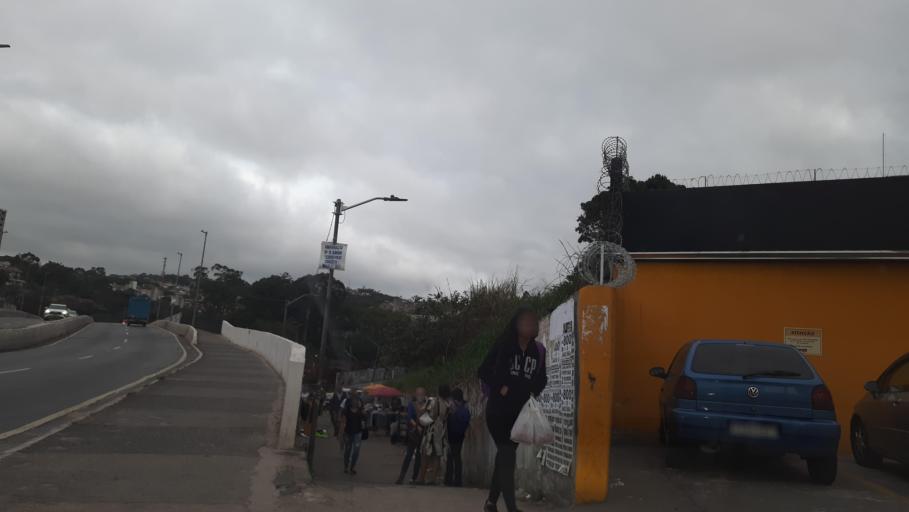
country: BR
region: Sao Paulo
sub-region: Caieiras
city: Caieiras
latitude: -23.4549
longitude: -46.7402
